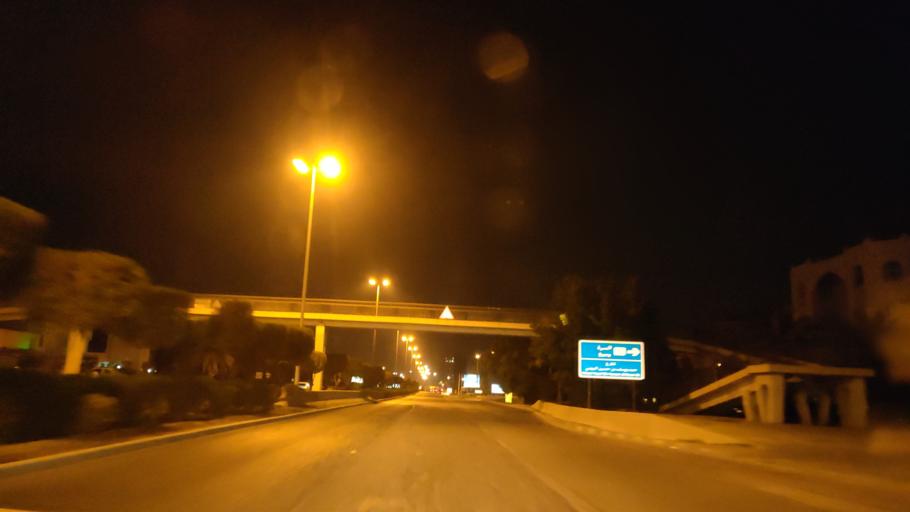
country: KW
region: Muhafazat Hawalli
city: Hawalli
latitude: 29.3211
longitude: 47.9985
